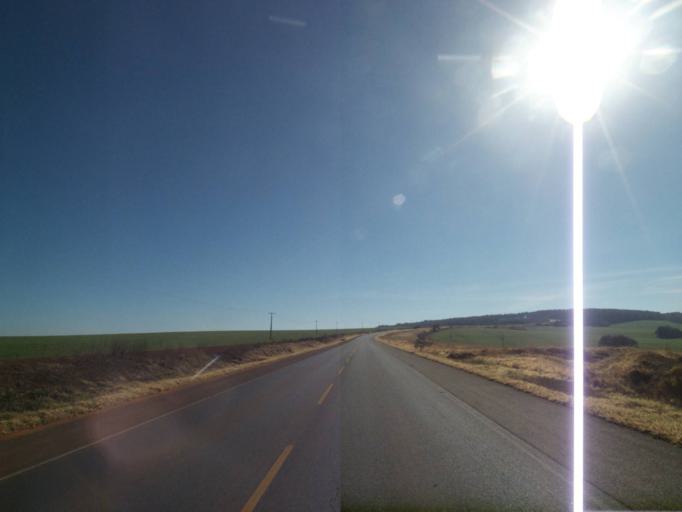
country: BR
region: Parana
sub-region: Tibagi
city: Tibagi
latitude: -24.4430
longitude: -50.4232
